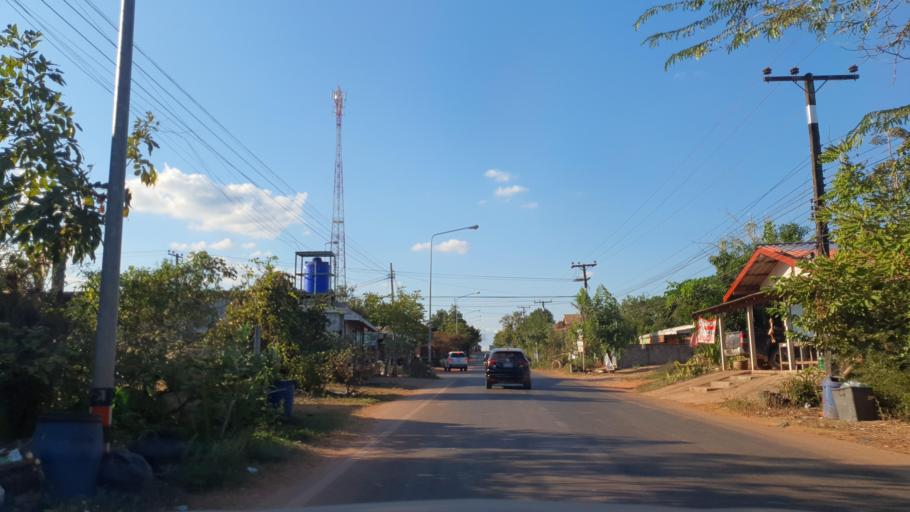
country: TH
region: Changwat Bueng Kan
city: Si Wilai
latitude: 18.1510
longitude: 103.9043
